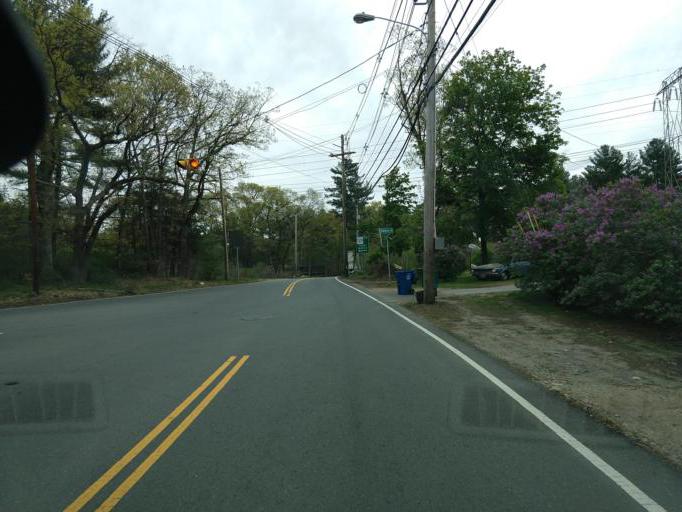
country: US
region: Massachusetts
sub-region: Middlesex County
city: Billerica
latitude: 42.5746
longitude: -71.2395
